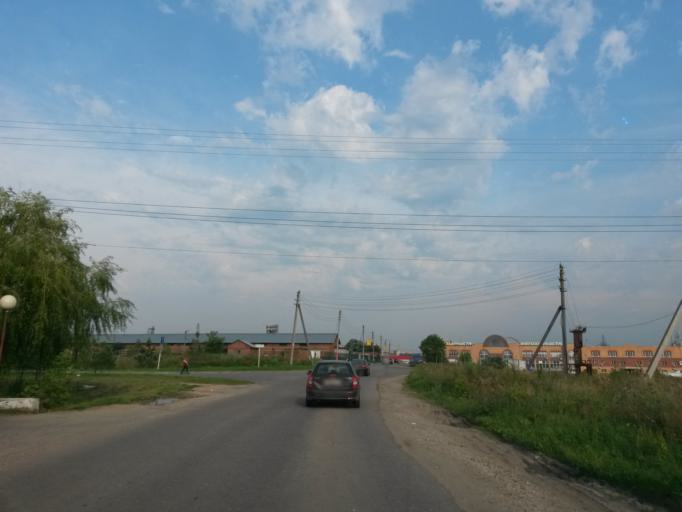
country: RU
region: Moskovskaya
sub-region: Podol'skiy Rayon
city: Podol'sk
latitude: 55.4470
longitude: 37.6234
